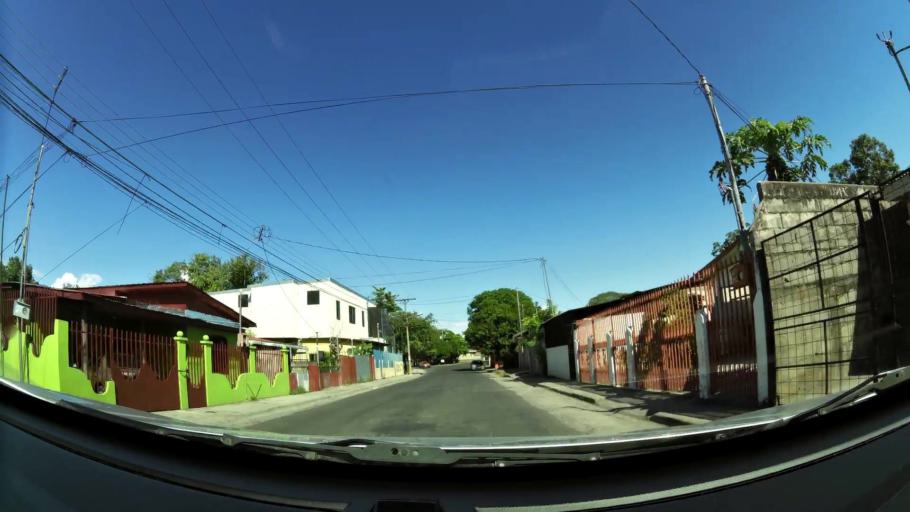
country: CR
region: Guanacaste
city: Liberia
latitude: 10.6347
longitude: -85.4387
